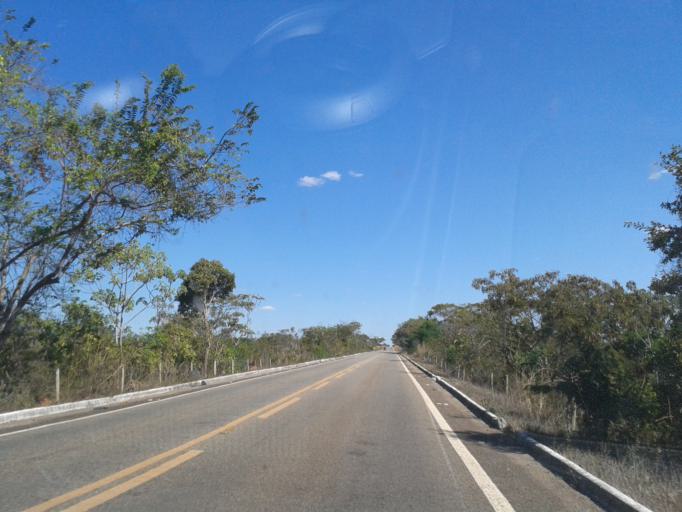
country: BR
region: Goias
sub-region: Sao Miguel Do Araguaia
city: Sao Miguel do Araguaia
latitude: -13.6333
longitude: -50.3128
